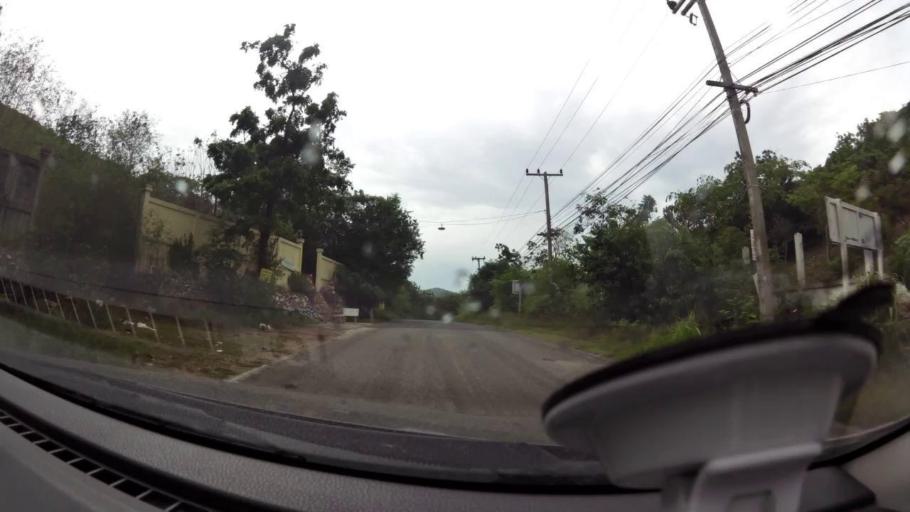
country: TH
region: Prachuap Khiri Khan
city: Pran Buri
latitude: 12.4388
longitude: 99.9712
